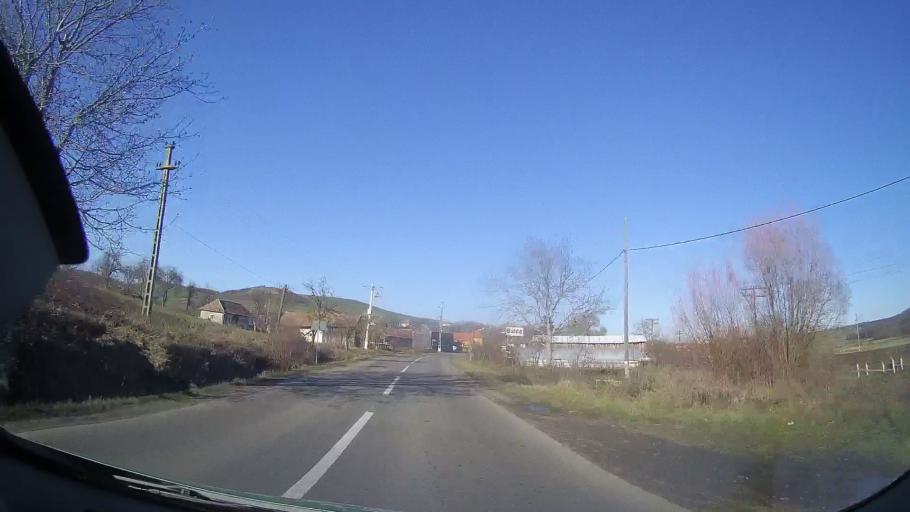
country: RO
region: Mures
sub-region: Comuna Sarmasu
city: Balda
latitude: 46.7226
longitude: 24.1436
